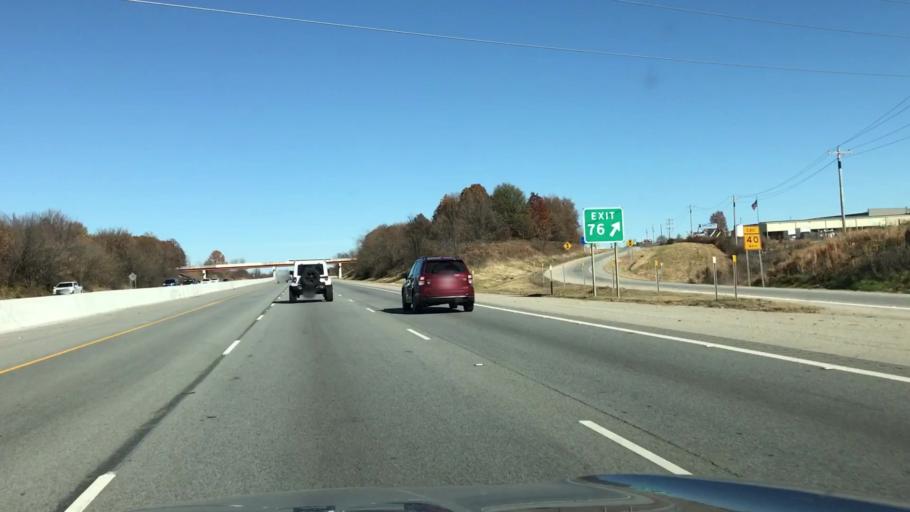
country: US
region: Arkansas
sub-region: Benton County
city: Bethel Heights
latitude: 36.2230
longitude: -94.1797
